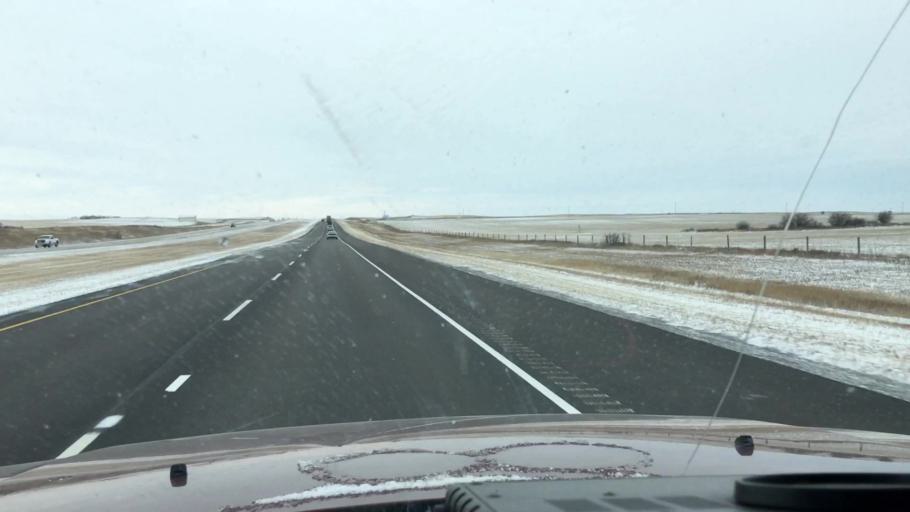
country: CA
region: Saskatchewan
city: Saskatoon
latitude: 51.7142
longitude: -106.4669
